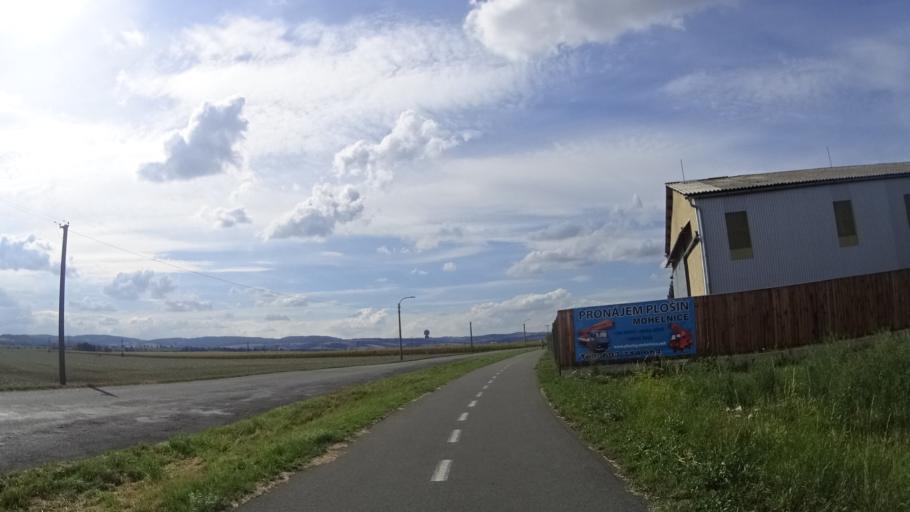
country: CZ
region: Olomoucky
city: Moravicany
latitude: 49.7591
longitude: 16.9549
